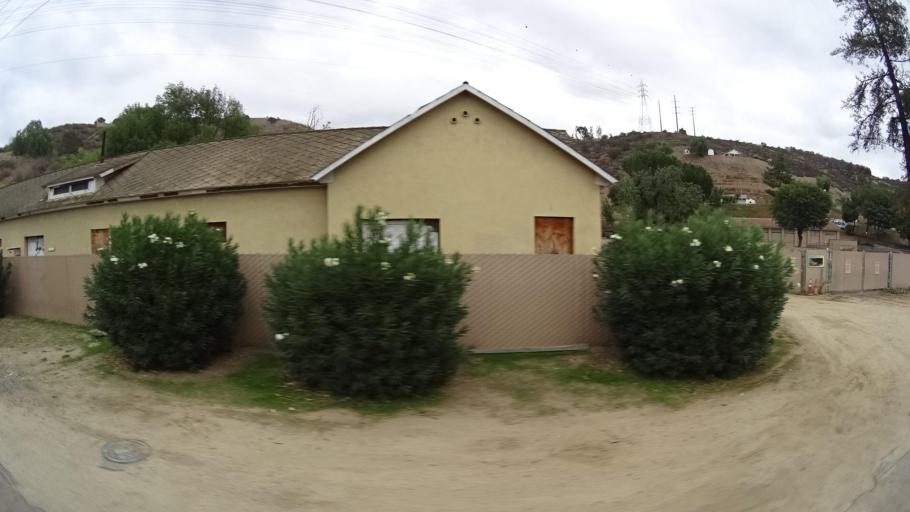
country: US
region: California
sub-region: San Diego County
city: Lakeside
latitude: 32.8672
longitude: -116.8940
